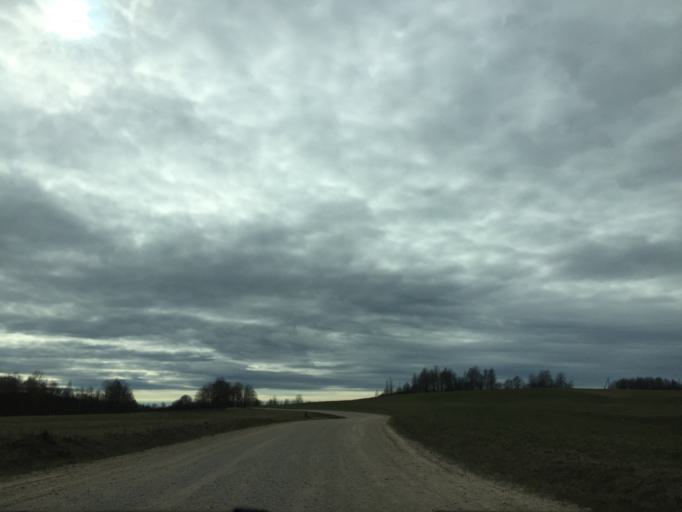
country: LT
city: Silale
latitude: 55.6136
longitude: 22.1861
